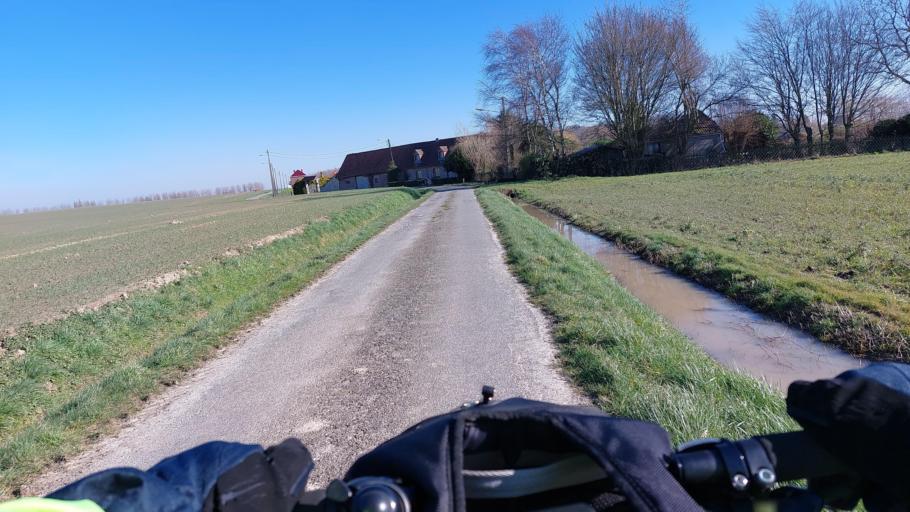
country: BE
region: Wallonia
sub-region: Province du Hainaut
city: Brugelette
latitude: 50.6174
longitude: 3.8636
